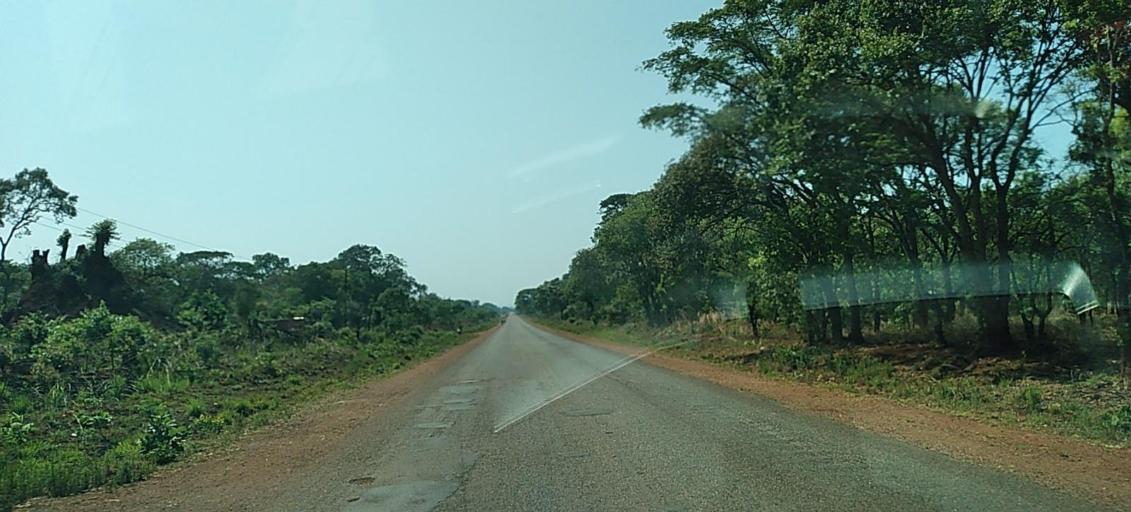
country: ZM
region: North-Western
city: Solwezi
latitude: -12.1226
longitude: 25.5163
